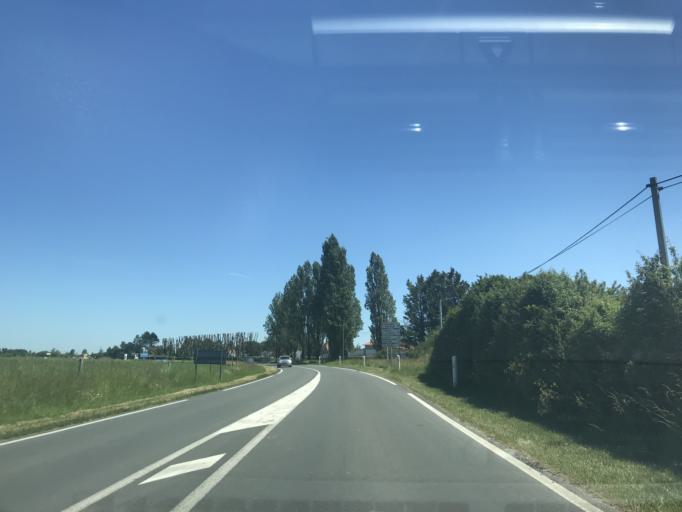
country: FR
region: Poitou-Charentes
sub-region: Departement de la Charente-Maritime
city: Meschers-sur-Gironde
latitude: 45.5625
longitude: -0.9449
